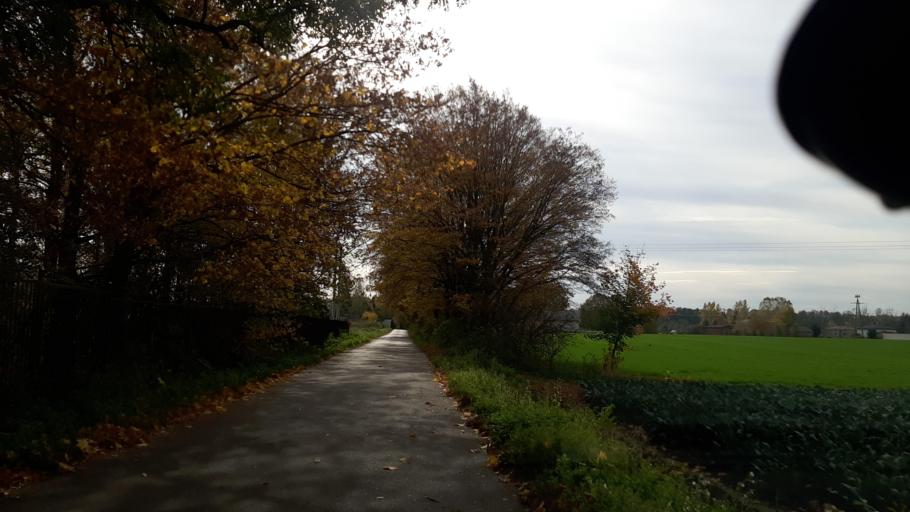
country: PL
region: Lublin Voivodeship
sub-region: Powiat pulawski
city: Markuszow
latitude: 51.3603
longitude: 22.2894
